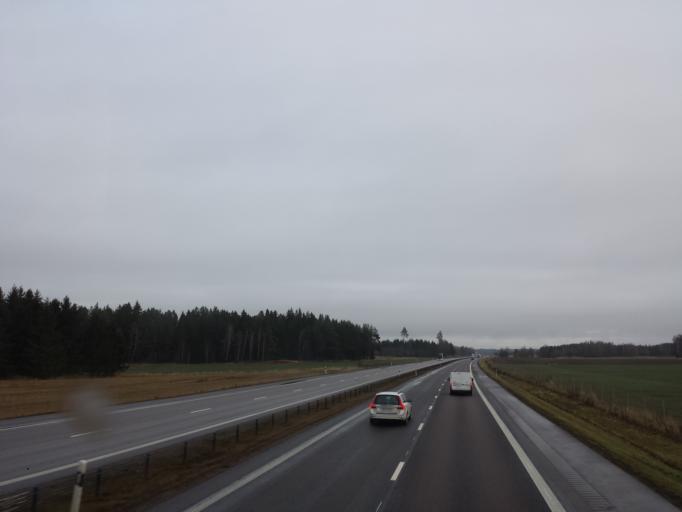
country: SE
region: OEstergoetland
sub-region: Linkopings Kommun
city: Vikingstad
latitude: 58.4019
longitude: 15.4390
